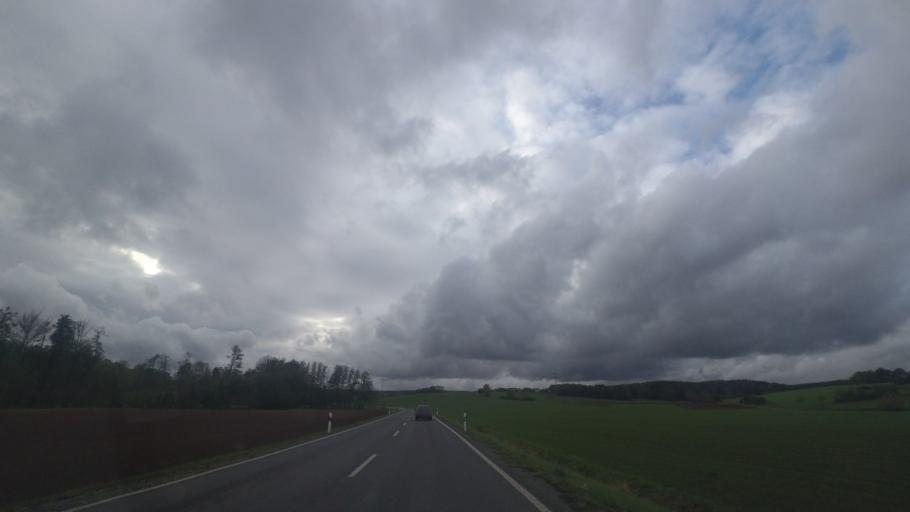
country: DE
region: Bavaria
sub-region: Regierungsbezirk Unterfranken
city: Hohenroth
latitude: 50.3295
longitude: 10.1843
